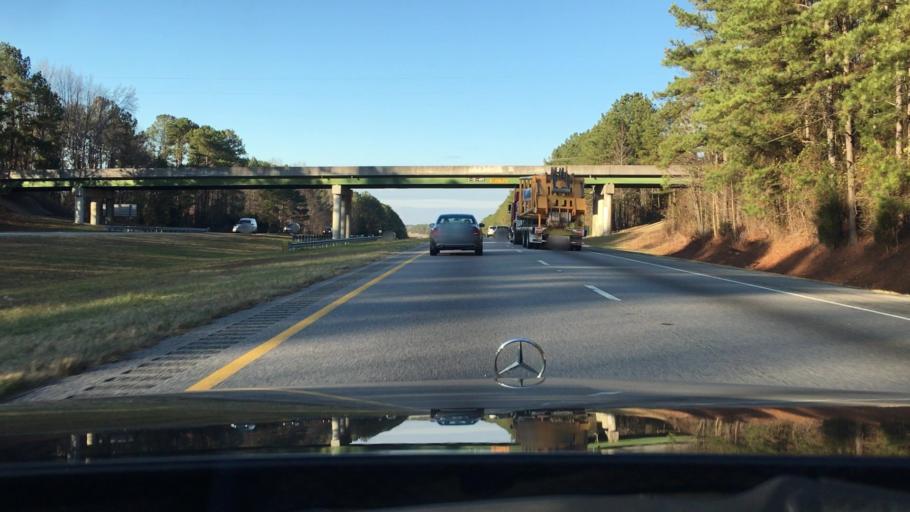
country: US
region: South Carolina
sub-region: Chester County
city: Eureka Mill
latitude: 34.6958
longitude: -81.0295
